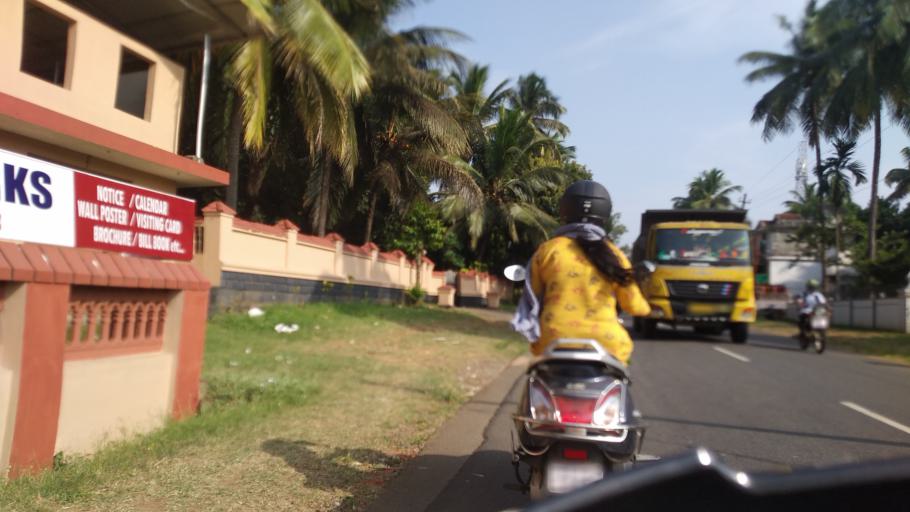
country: IN
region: Kerala
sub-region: Thrissur District
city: Chelakara
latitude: 10.5994
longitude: 76.4961
